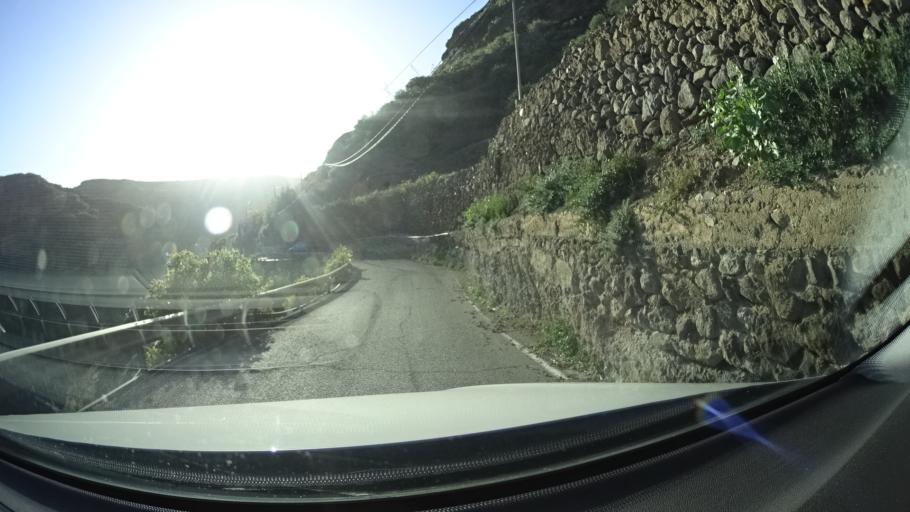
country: ES
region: Canary Islands
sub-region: Provincia de Las Palmas
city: Artenara
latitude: 28.0464
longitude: -15.6615
